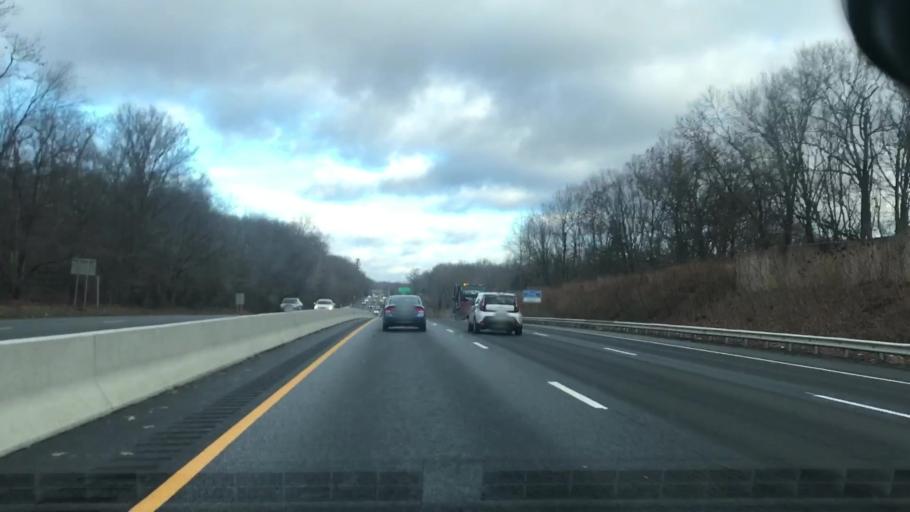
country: US
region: New Jersey
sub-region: Bergen County
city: Saddle River
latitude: 41.0239
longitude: -74.1093
